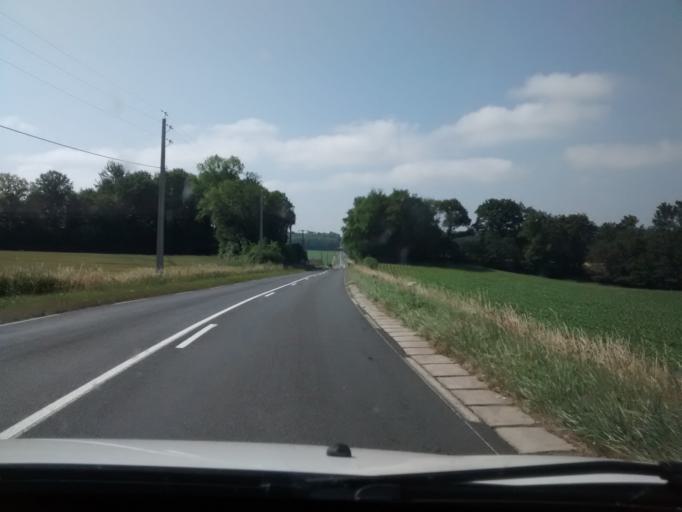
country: FR
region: Pays de la Loire
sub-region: Departement de la Sarthe
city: Vibraye
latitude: 48.1082
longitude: 0.7160
